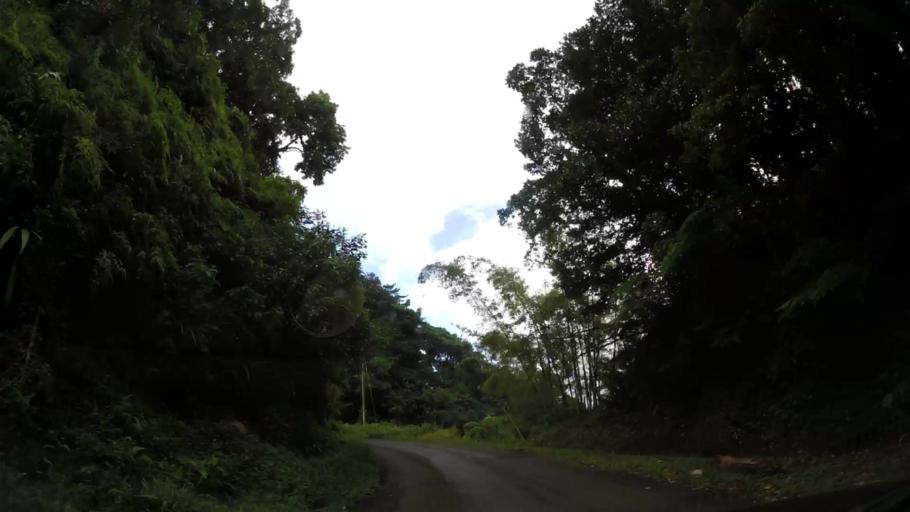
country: DM
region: Saint Paul
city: Pont Casse
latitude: 15.3970
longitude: -61.3104
